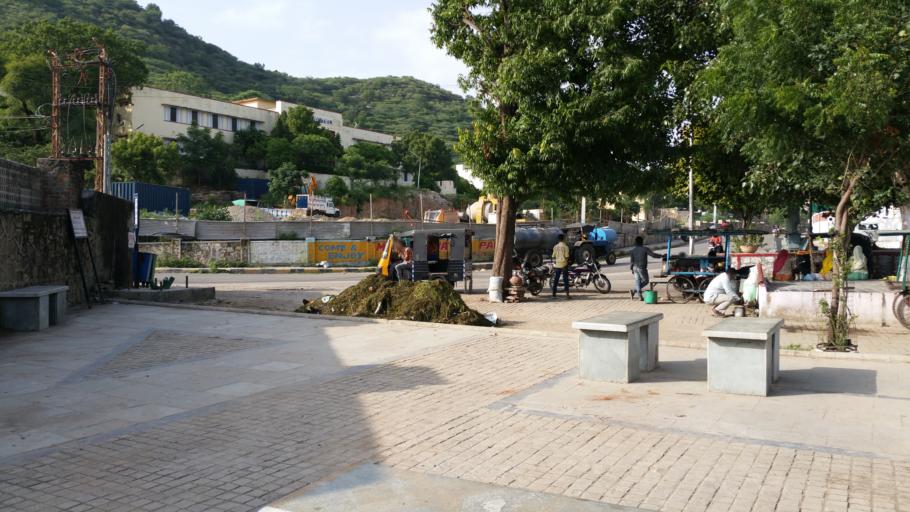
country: IN
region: Rajasthan
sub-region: Udaipur
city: Udaipur
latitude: 24.6090
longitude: 73.6774
